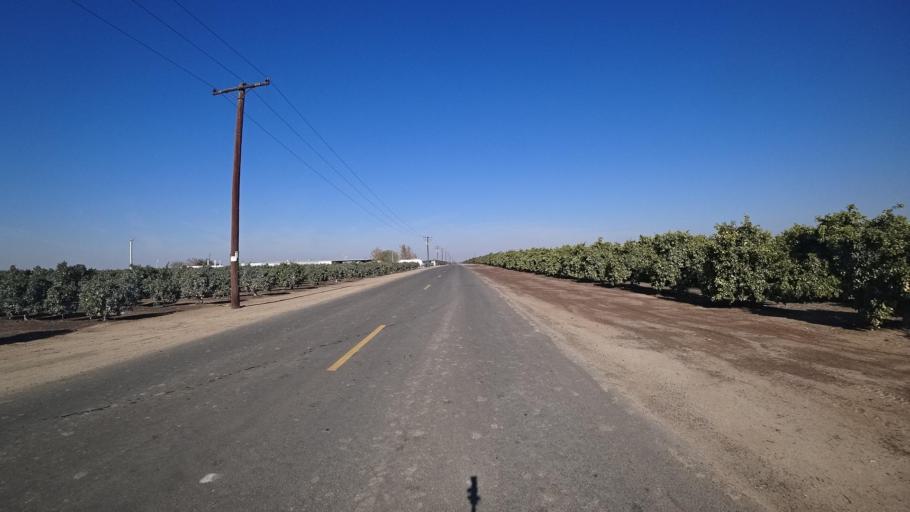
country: US
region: California
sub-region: Tulare County
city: Richgrove
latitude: 35.7217
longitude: -119.1340
